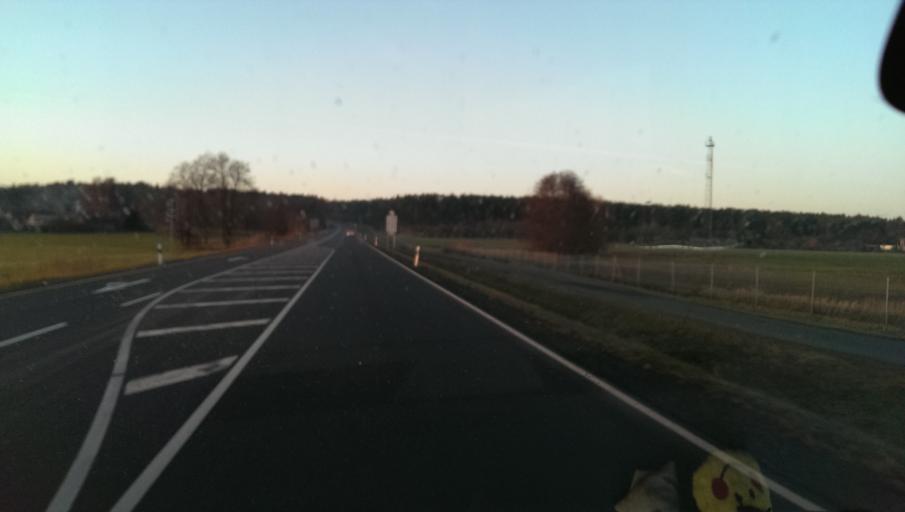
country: DE
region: Brandenburg
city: Falkenberg
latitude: 51.6399
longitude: 13.3074
